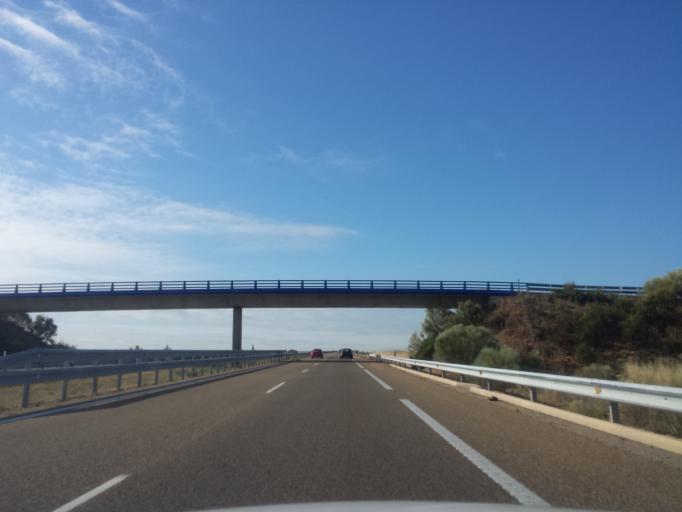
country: ES
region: Castille and Leon
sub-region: Provincia de Leon
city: Valdevimbre
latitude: 42.3840
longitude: -5.5955
